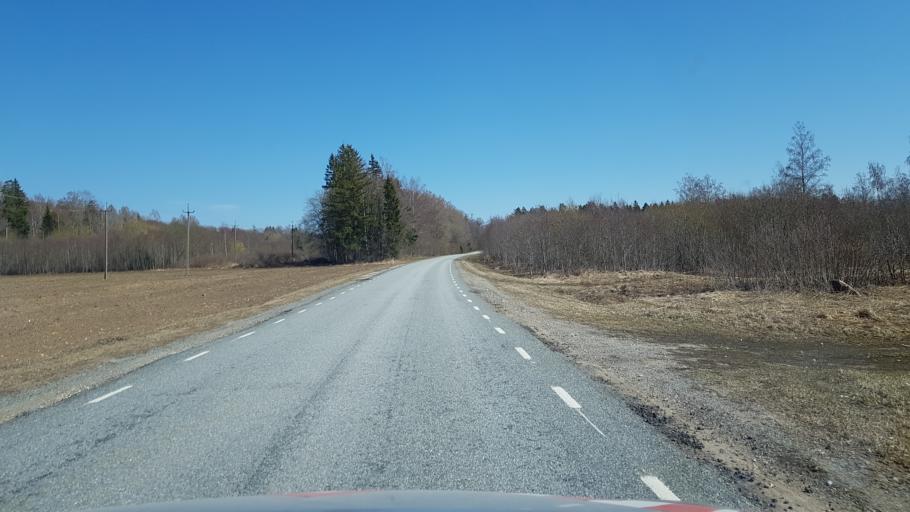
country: EE
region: Laeaene-Virumaa
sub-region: Vaeike-Maarja vald
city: Vaike-Maarja
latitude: 59.1249
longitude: 26.2922
